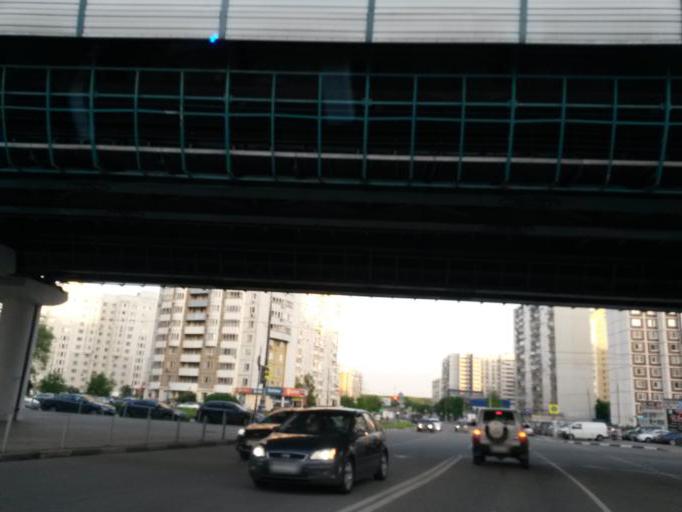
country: RU
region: Moskovskaya
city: Shcherbinka
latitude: 55.5484
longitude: 37.5550
